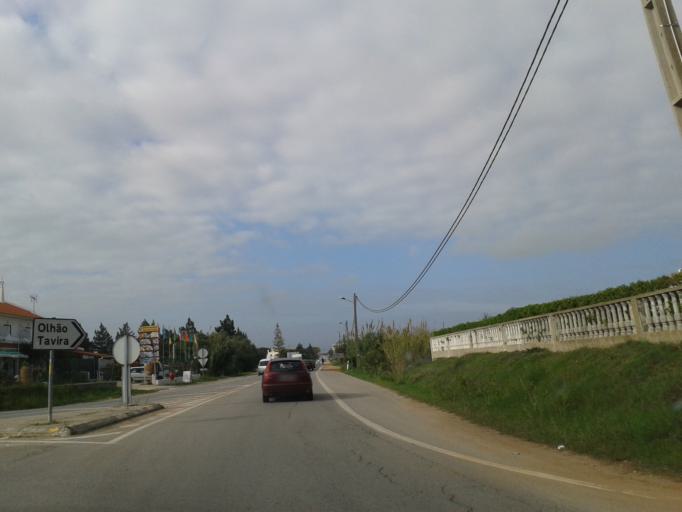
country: PT
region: Faro
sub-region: Vila Real de Santo Antonio
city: Monte Gordo
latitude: 37.1817
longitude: -7.4948
